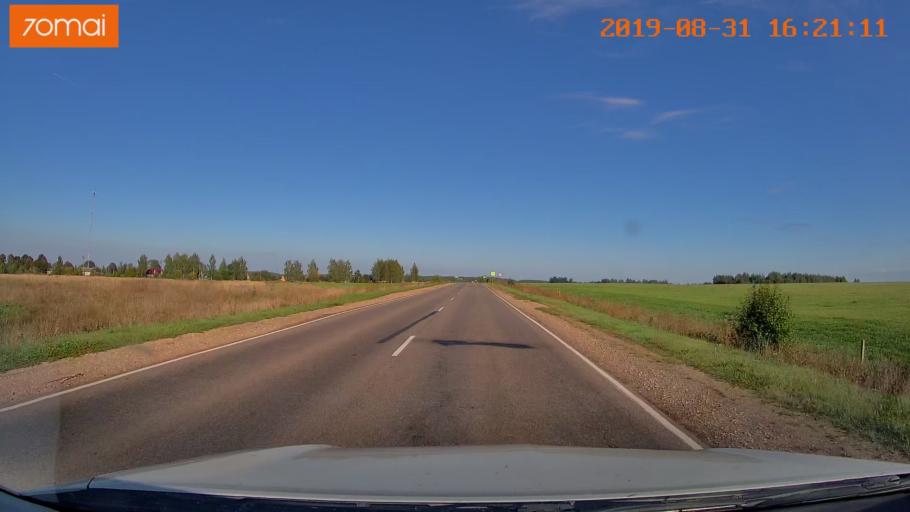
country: RU
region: Kaluga
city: Babynino
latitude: 54.5224
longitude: 35.6248
